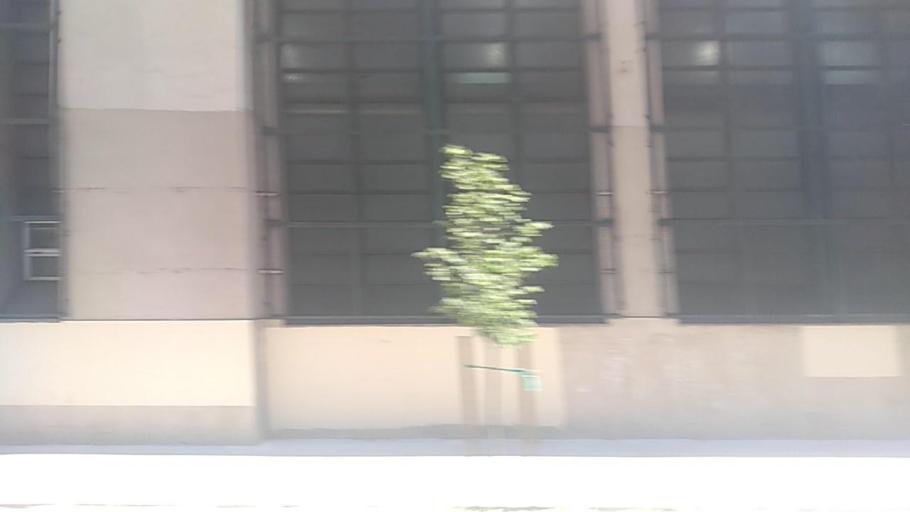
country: AR
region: Buenos Aires F.D.
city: Villa Santa Rita
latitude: -34.6046
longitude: -58.5099
